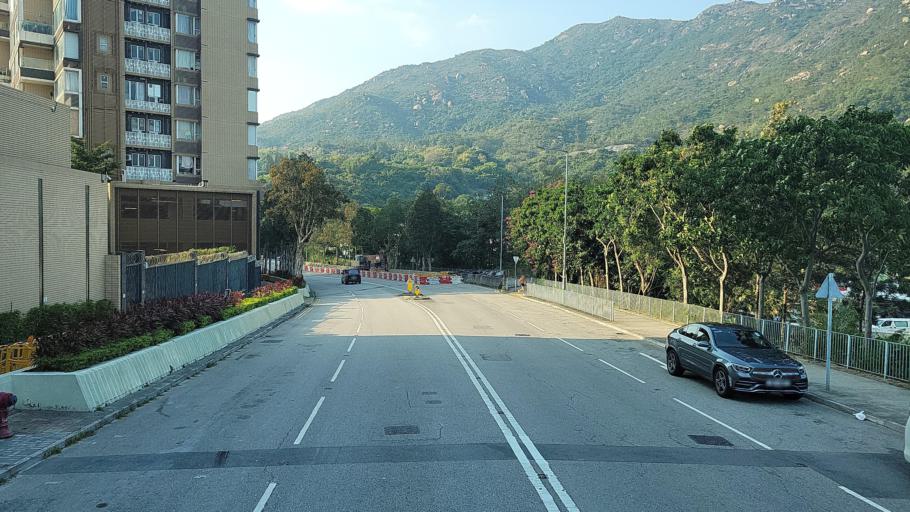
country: HK
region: Tuen Mun
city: Tuen Mun
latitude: 22.3749
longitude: 114.0018
